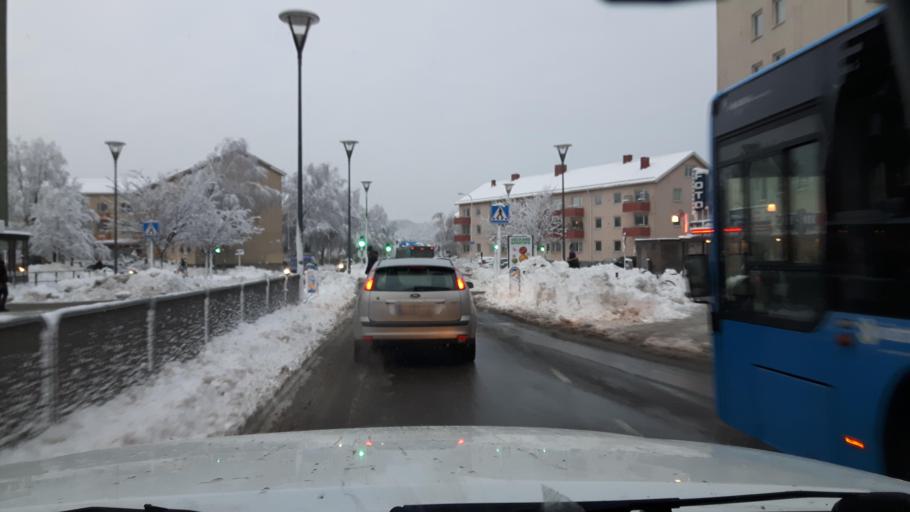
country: SE
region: Vaestra Goetaland
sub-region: Goteborg
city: Majorna
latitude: 57.7213
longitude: 11.9346
